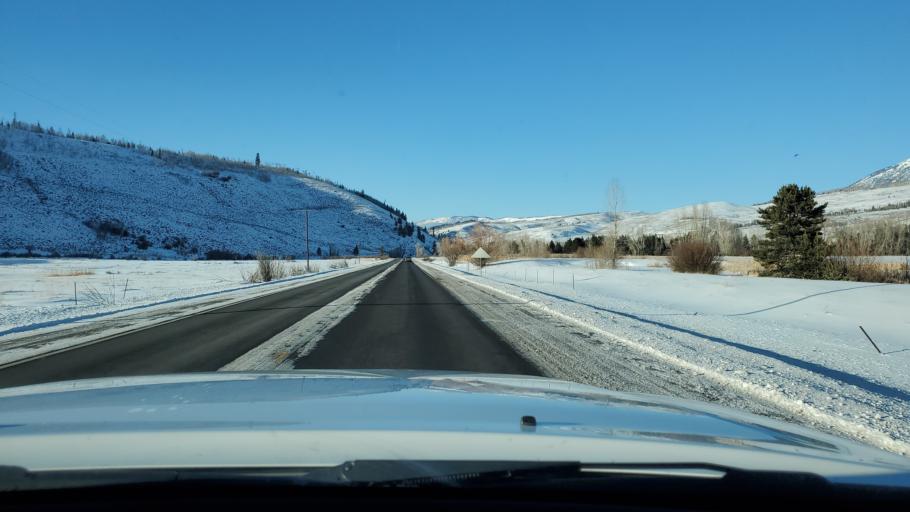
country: US
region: Colorado
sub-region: Summit County
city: Silverthorne
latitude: 39.6996
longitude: -106.1090
